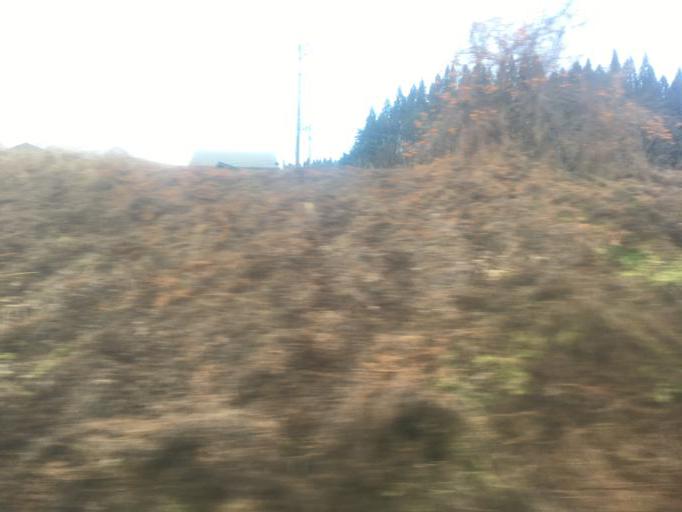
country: JP
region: Akita
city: Takanosu
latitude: 40.2214
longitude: 140.3266
